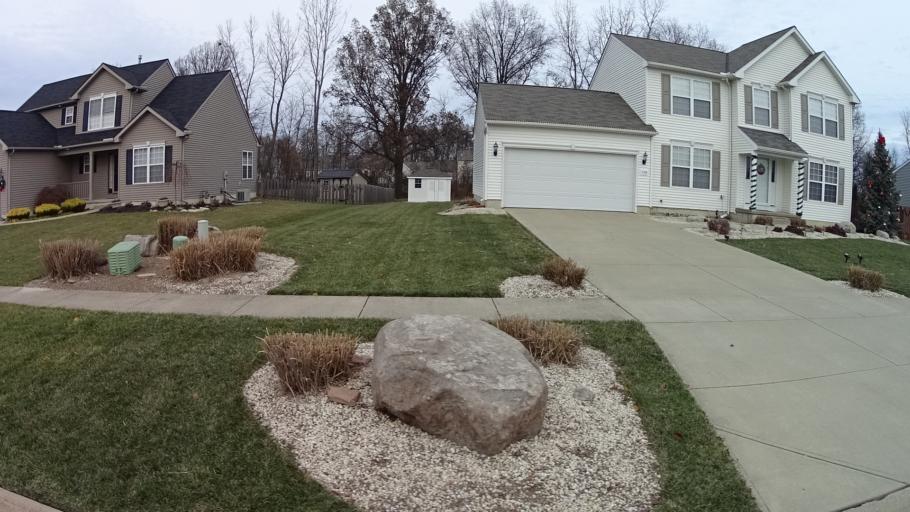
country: US
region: Ohio
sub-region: Lorain County
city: North Ridgeville
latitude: 41.4017
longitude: -82.0374
